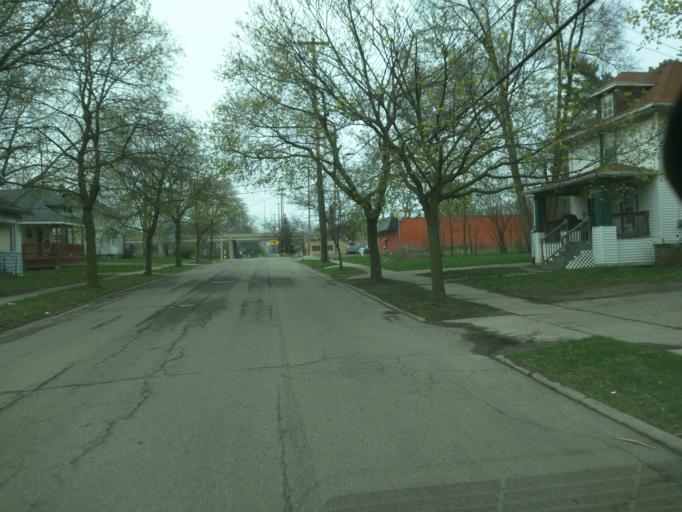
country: US
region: Michigan
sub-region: Ingham County
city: Lansing
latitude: 42.7247
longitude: -84.5331
